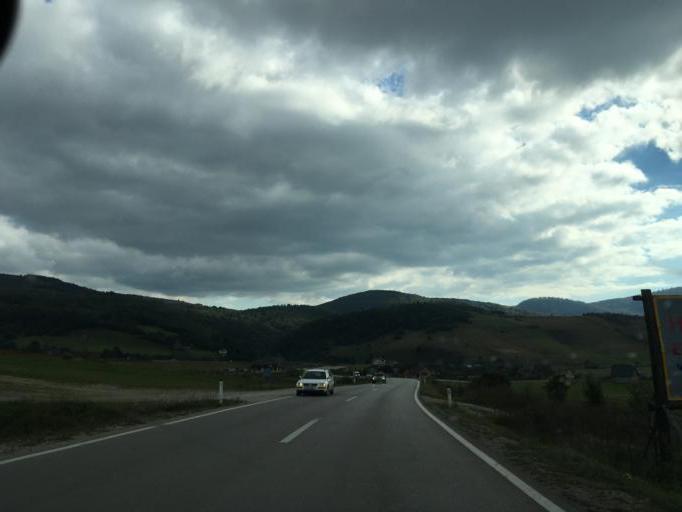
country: BA
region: Federation of Bosnia and Herzegovina
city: Novi Travnik
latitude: 44.1077
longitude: 17.5756
